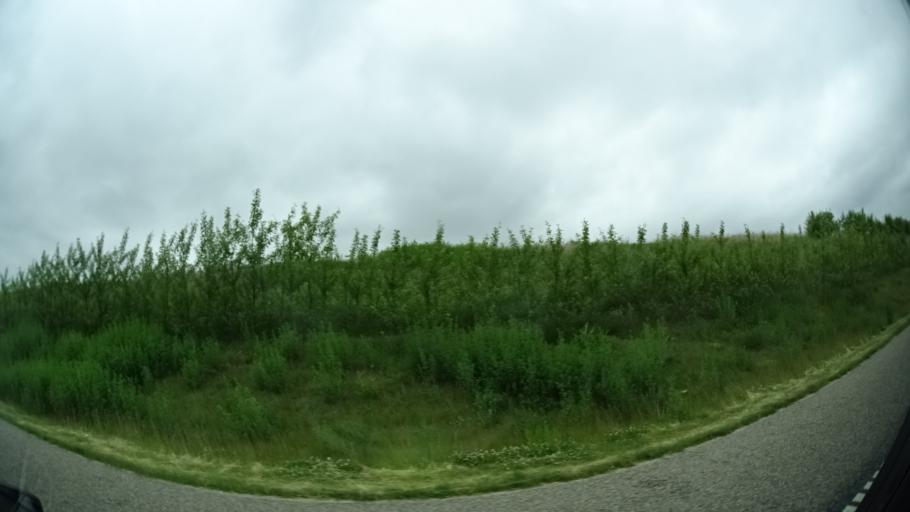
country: DK
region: Central Jutland
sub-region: Arhus Kommune
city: Trige
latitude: 56.2167
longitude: 10.1822
